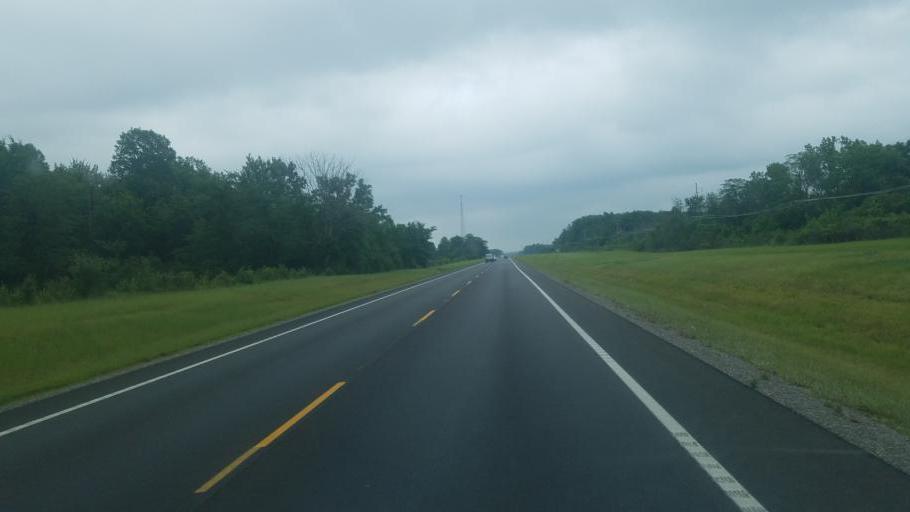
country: US
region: Ohio
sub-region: Logan County
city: Russells Point
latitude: 40.4612
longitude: -83.8654
